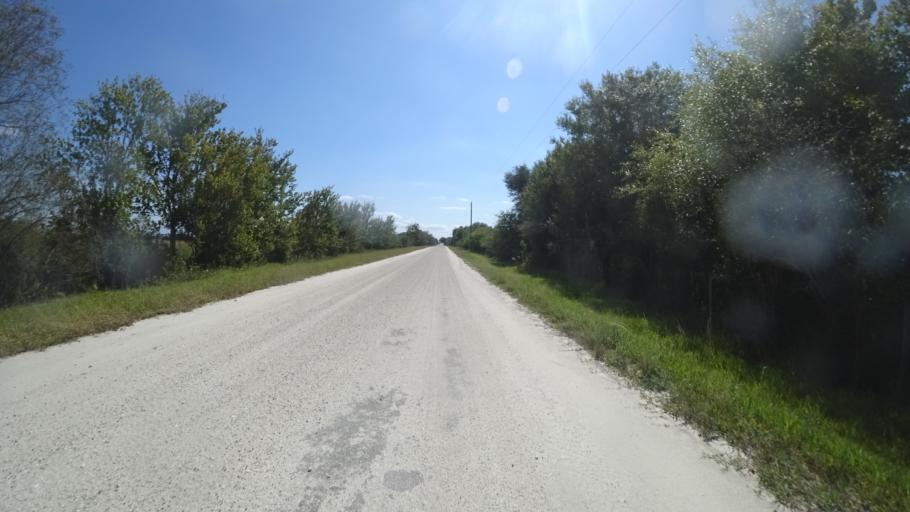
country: US
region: Florida
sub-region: DeSoto County
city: Arcadia
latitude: 27.3196
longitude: -82.0805
